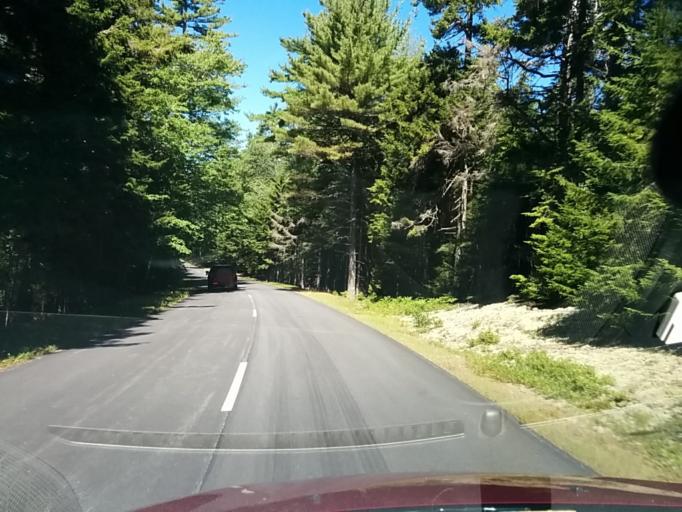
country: US
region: Maine
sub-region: Hancock County
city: Bar Harbor
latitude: 44.3051
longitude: -68.2182
